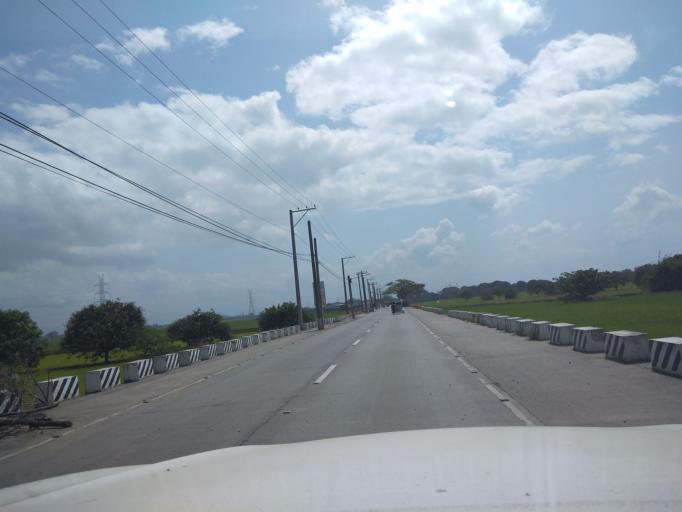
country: PH
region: Central Luzon
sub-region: Province of Pampanga
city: Talang
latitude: 15.0256
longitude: 120.8383
